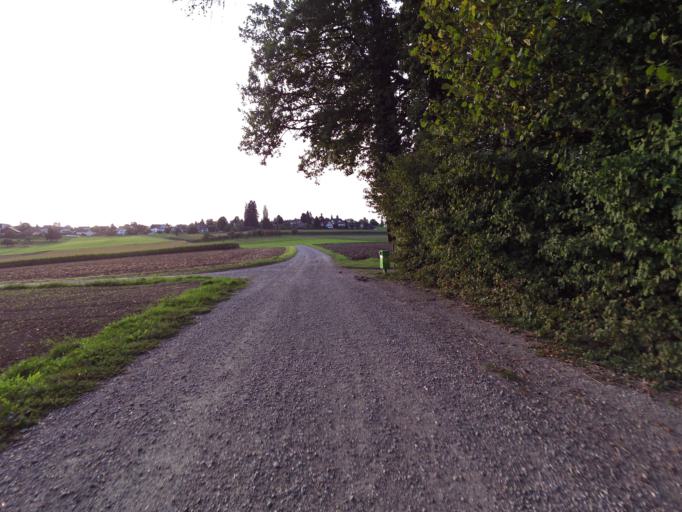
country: CH
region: Thurgau
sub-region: Frauenfeld District
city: Frauenfeld
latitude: 47.5388
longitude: 8.8854
